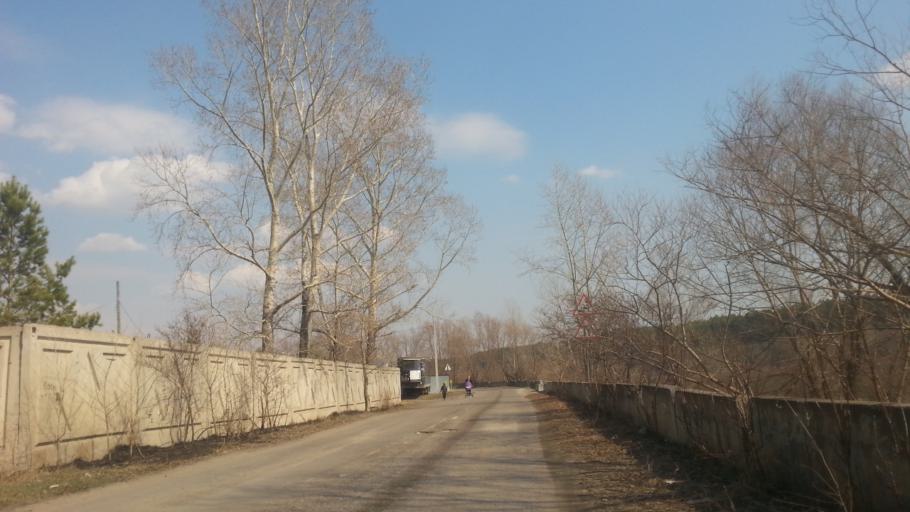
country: RU
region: Altai Krai
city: Yuzhnyy
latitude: 53.3087
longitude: 83.7189
